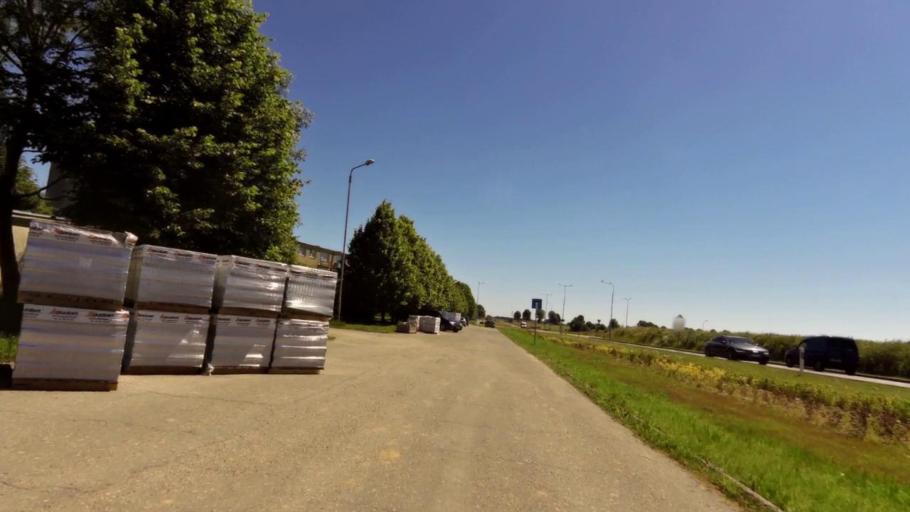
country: PL
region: West Pomeranian Voivodeship
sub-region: Powiat kolobrzeski
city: Goscino
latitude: 54.0508
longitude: 15.6470
